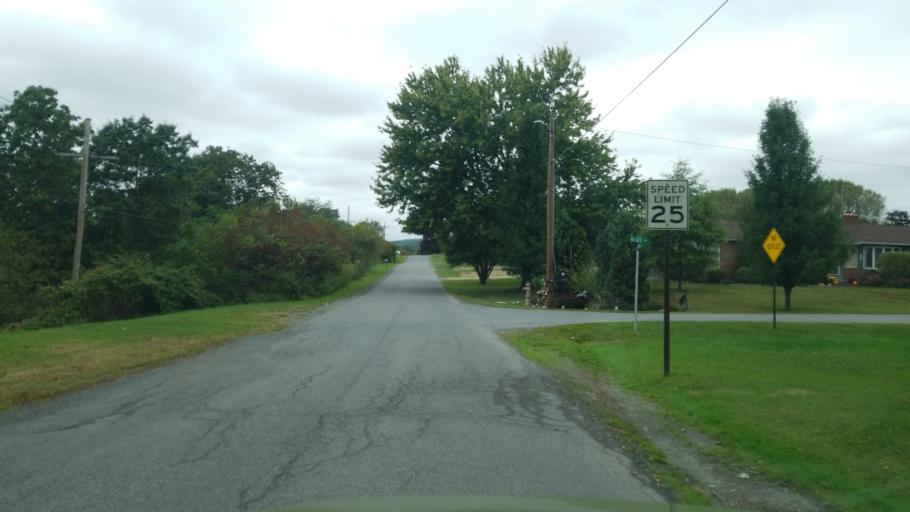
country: US
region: Pennsylvania
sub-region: Clearfield County
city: Curwensville
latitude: 40.9694
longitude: -78.5089
